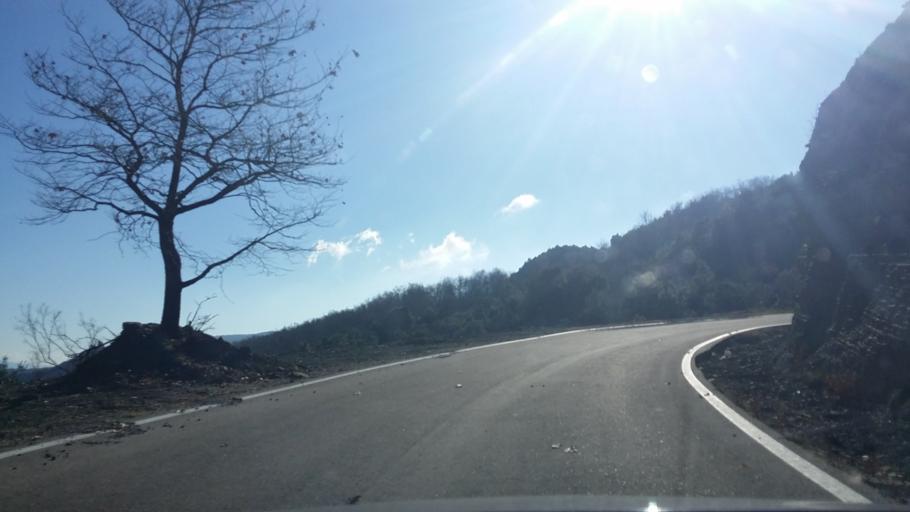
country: GR
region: West Greece
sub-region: Nomos Aitolias kai Akarnanias
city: Krikellos
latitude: 38.9889
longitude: 21.2782
